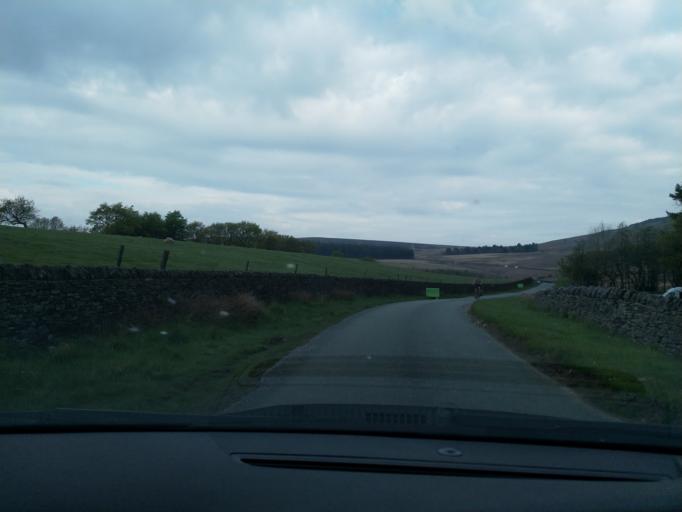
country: GB
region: England
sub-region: Derbyshire
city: Hathersage
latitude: 53.3496
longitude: -1.6446
